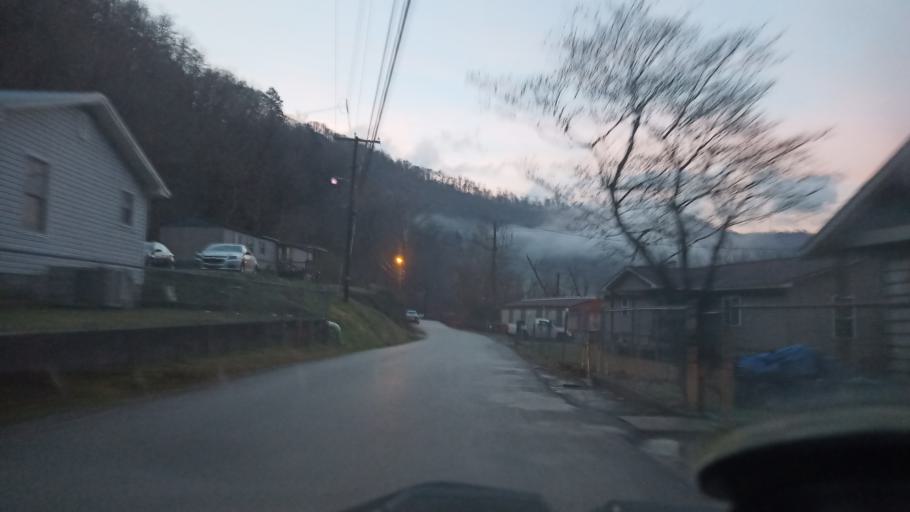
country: US
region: West Virginia
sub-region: Logan County
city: Mallory
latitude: 37.7252
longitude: -81.8764
